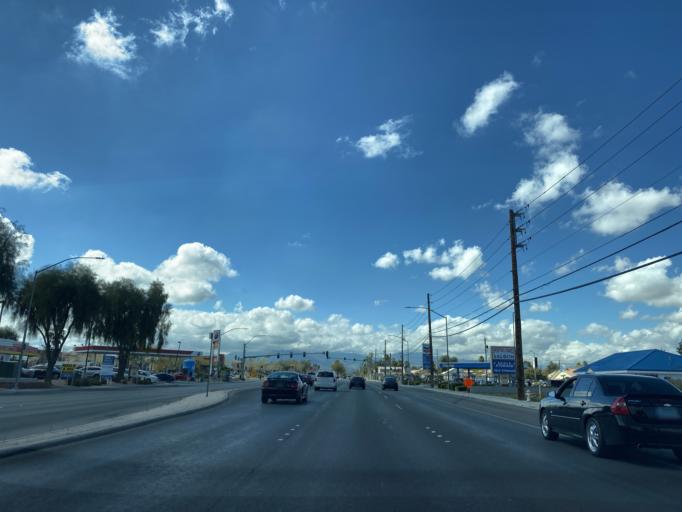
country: US
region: Nevada
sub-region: Clark County
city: North Las Vegas
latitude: 36.2395
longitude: -115.1782
